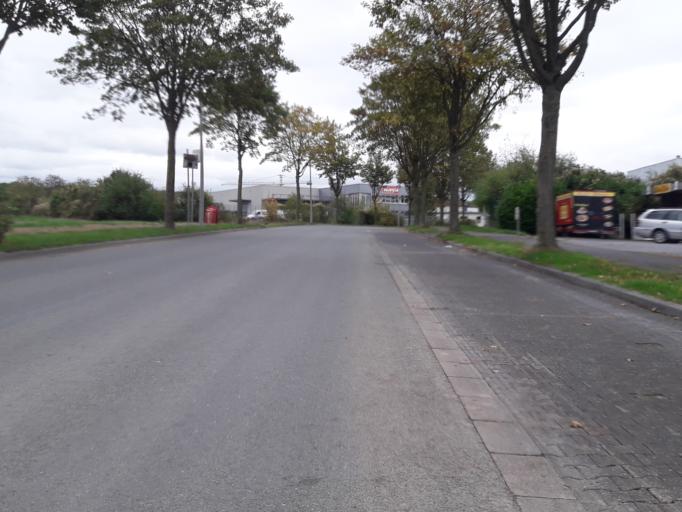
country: DE
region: North Rhine-Westphalia
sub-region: Regierungsbezirk Detmold
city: Paderborn
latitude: 51.6924
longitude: 8.7457
